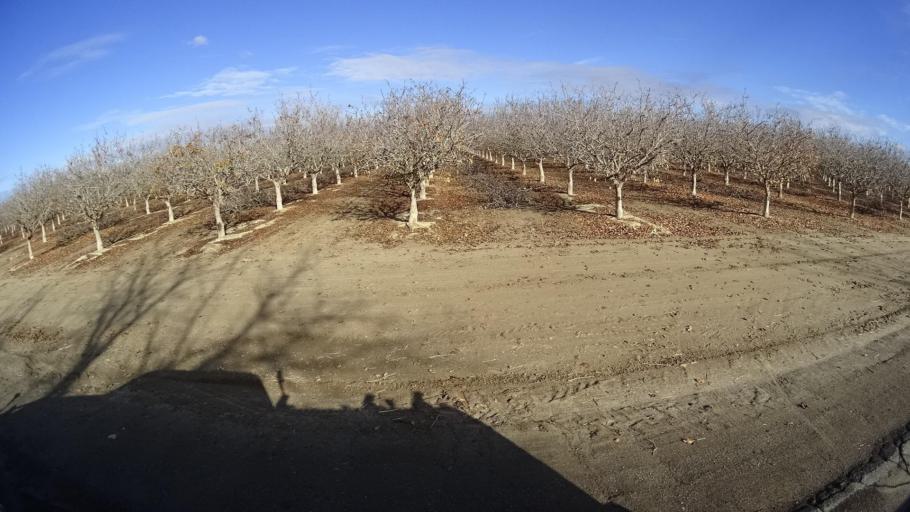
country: US
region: California
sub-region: Kern County
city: Shafter
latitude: 35.3836
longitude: -119.2642
